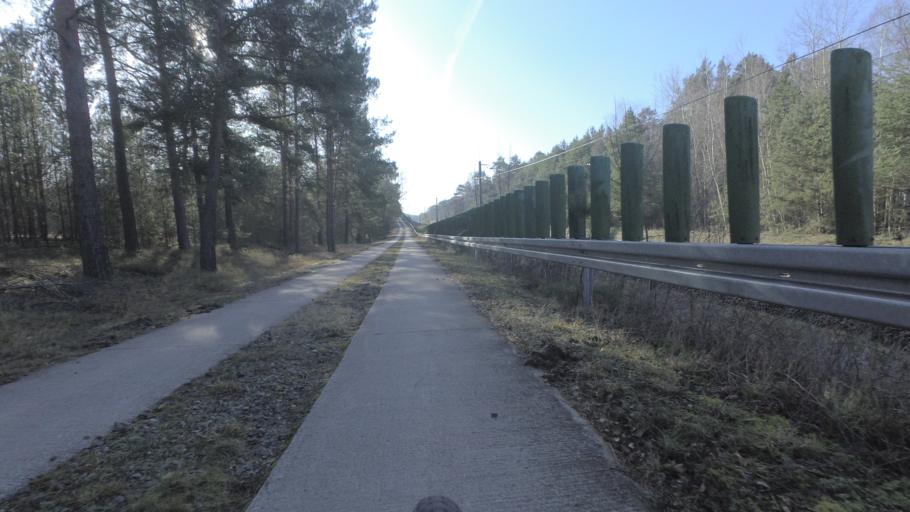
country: DE
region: Brandenburg
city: Trebbin
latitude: 52.1512
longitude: 13.2199
